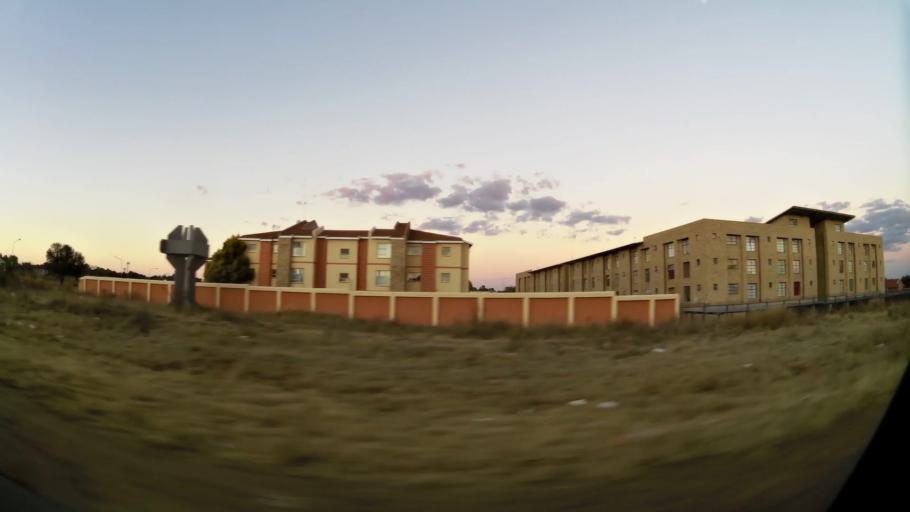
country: ZA
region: North-West
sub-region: Dr Kenneth Kaunda District Municipality
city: Potchefstroom
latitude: -26.6902
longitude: 27.0777
